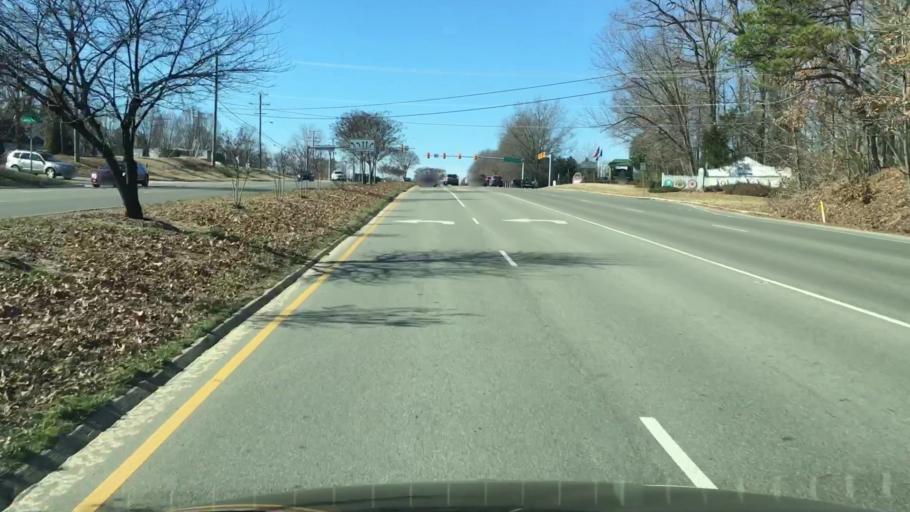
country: US
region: Virginia
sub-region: Chesterfield County
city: Brandermill
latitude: 37.5027
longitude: -77.6385
